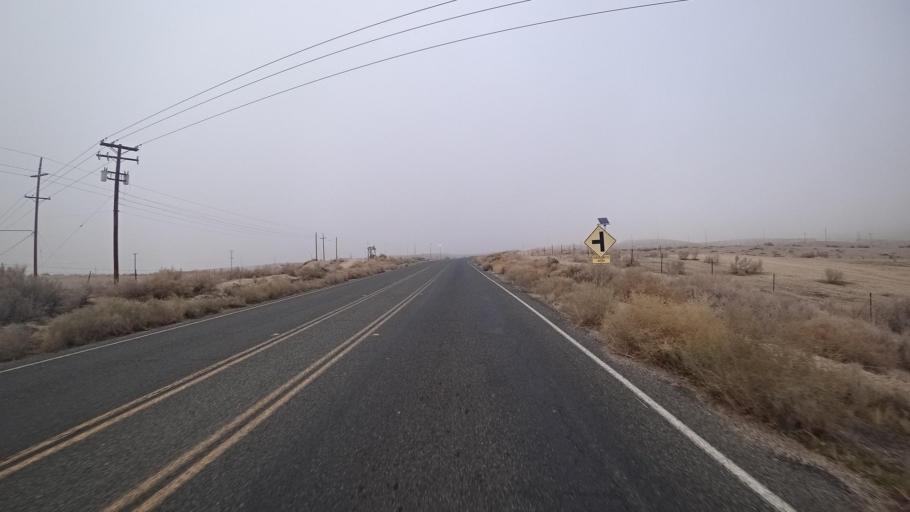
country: US
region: California
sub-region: Kern County
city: Ford City
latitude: 35.2675
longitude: -119.4663
